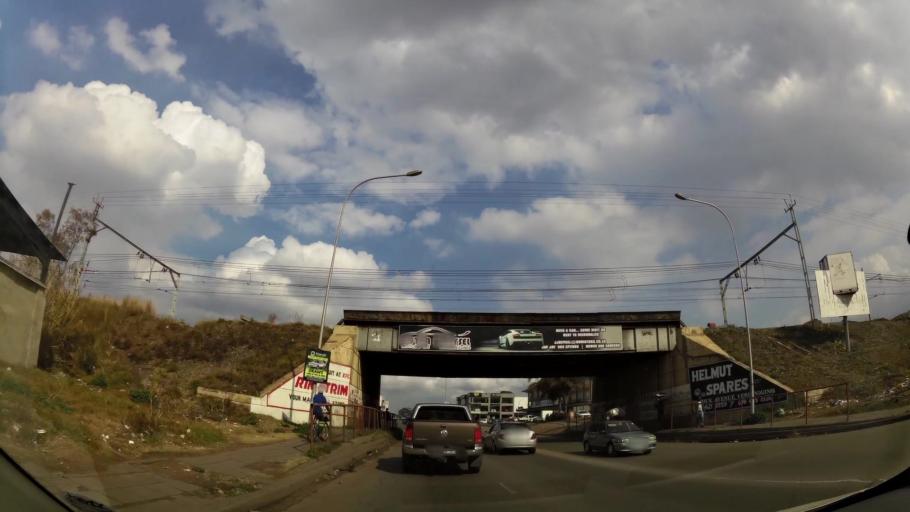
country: ZA
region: Gauteng
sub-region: Sedibeng District Municipality
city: Vereeniging
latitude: -26.6658
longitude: 27.9338
